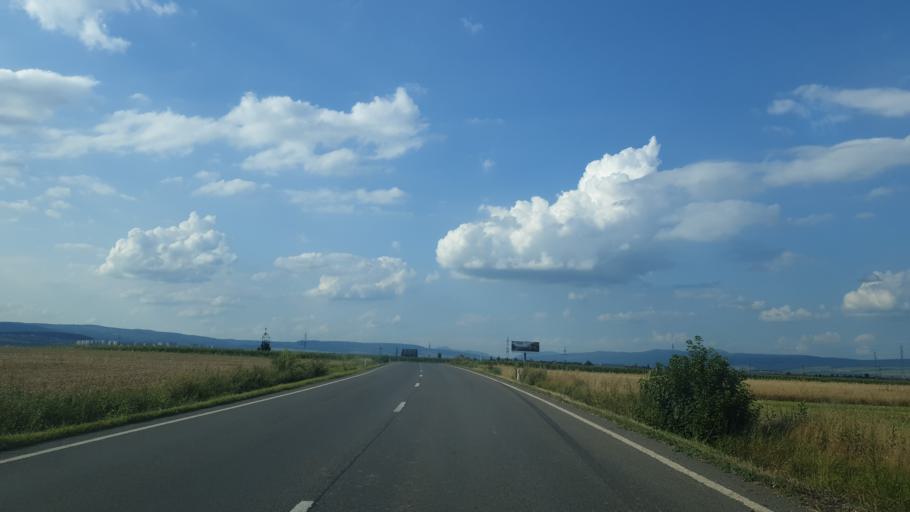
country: RO
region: Covasna
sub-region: Comuna Chichis
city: Chichis
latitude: 45.8188
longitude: 25.7996
